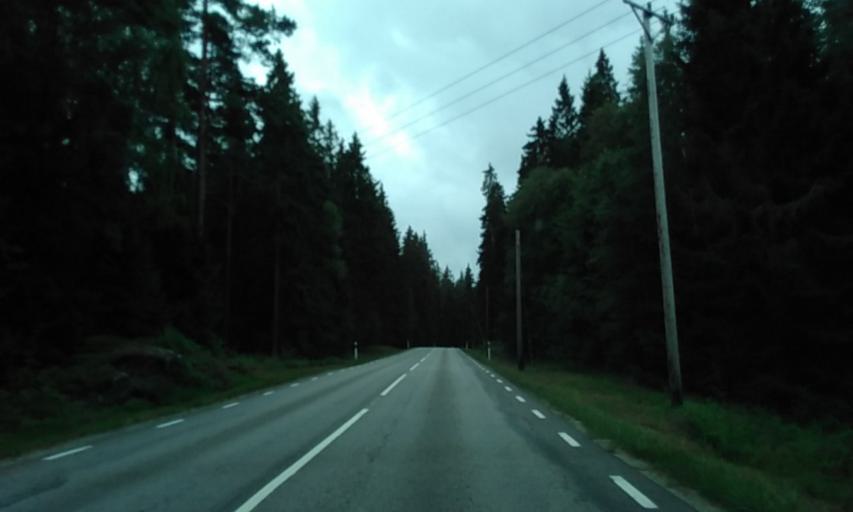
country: SE
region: Vaestra Goetaland
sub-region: Alingsas Kommun
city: Alingsas
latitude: 57.8574
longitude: 12.6161
